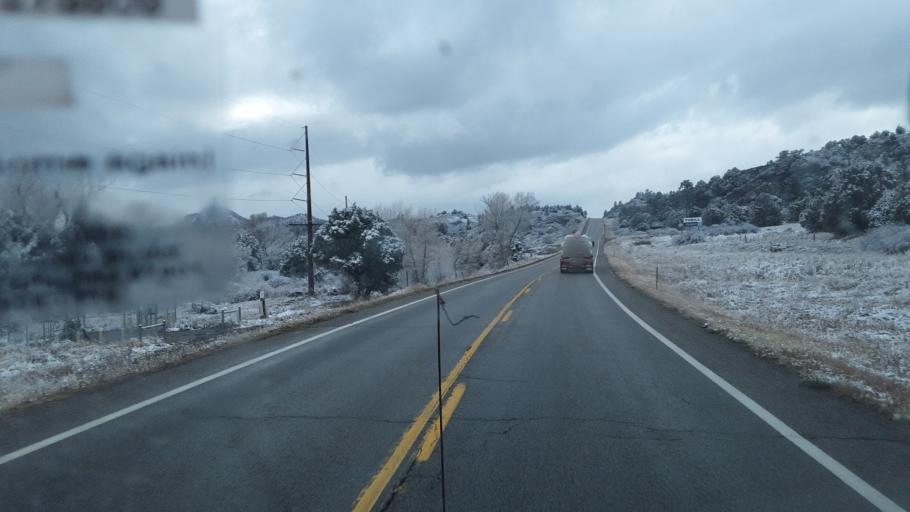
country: US
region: Colorado
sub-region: Archuleta County
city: Pagosa Springs
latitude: 37.2077
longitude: -107.2469
